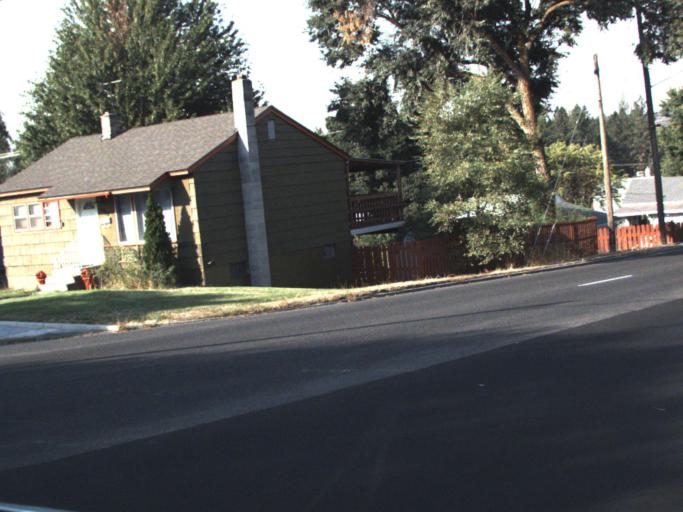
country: US
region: Washington
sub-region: Spokane County
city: Town and Country
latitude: 47.7154
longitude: -117.4731
